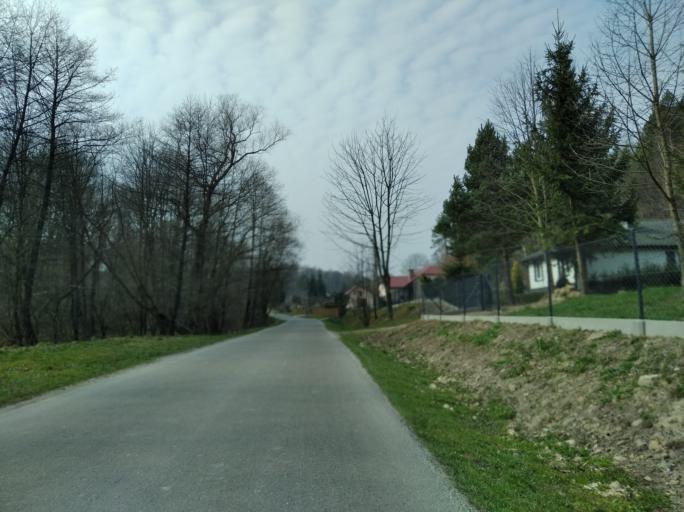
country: PL
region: Subcarpathian Voivodeship
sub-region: Powiat strzyzowski
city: Strzyzow
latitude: 49.7996
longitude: 21.8219
